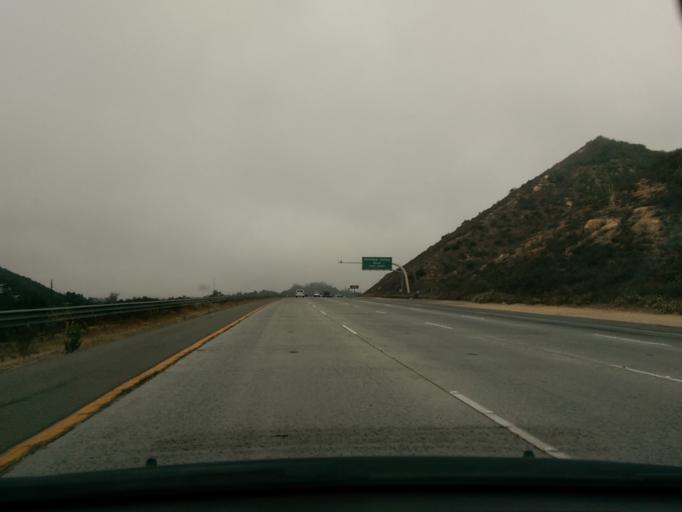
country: US
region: California
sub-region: San Diego County
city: Rainbow
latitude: 33.4401
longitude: -117.1386
